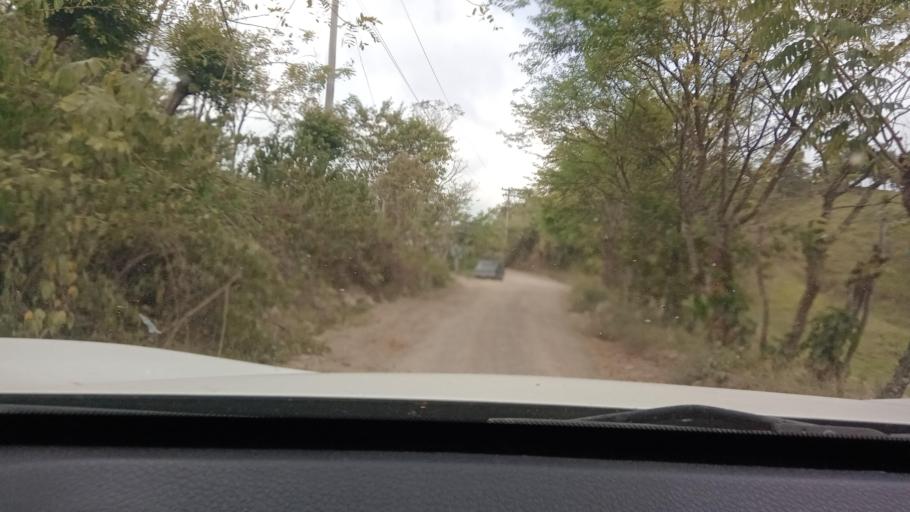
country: MX
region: Tabasco
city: Chontalpa
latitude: 17.5036
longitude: -93.6423
